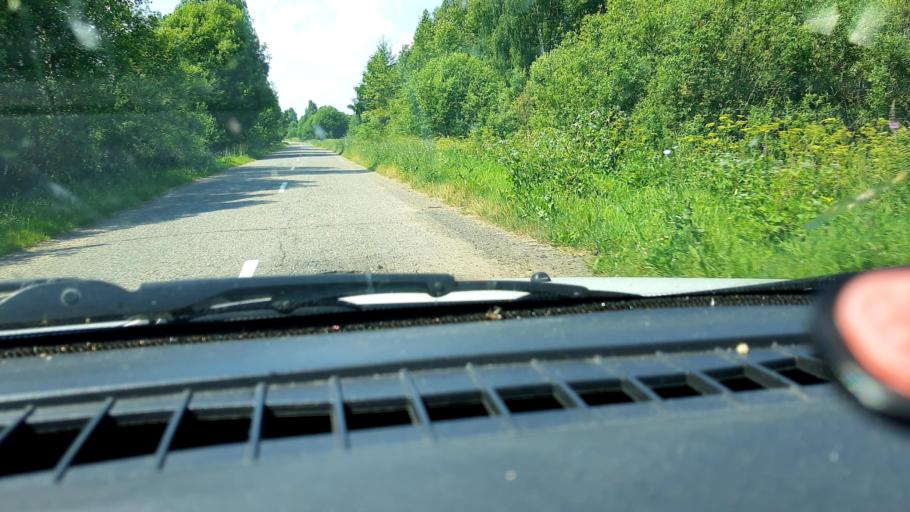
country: RU
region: Nizjnij Novgorod
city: Sharanga
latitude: 57.0558
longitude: 46.5730
